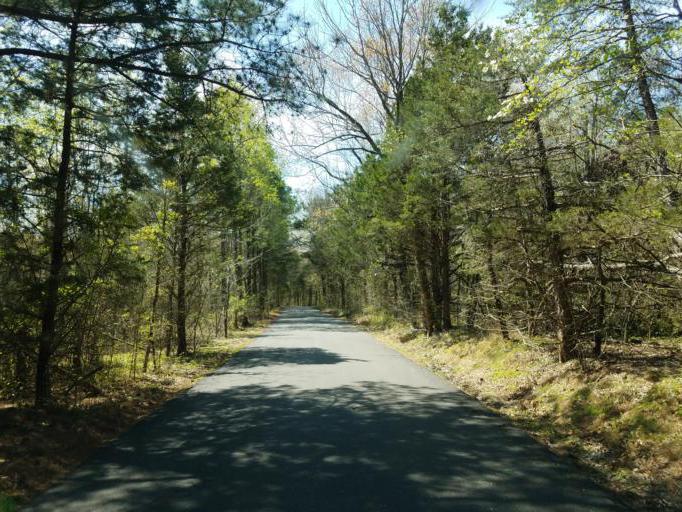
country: US
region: Kentucky
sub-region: Barren County
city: Cave City
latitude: 37.1641
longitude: -86.0394
